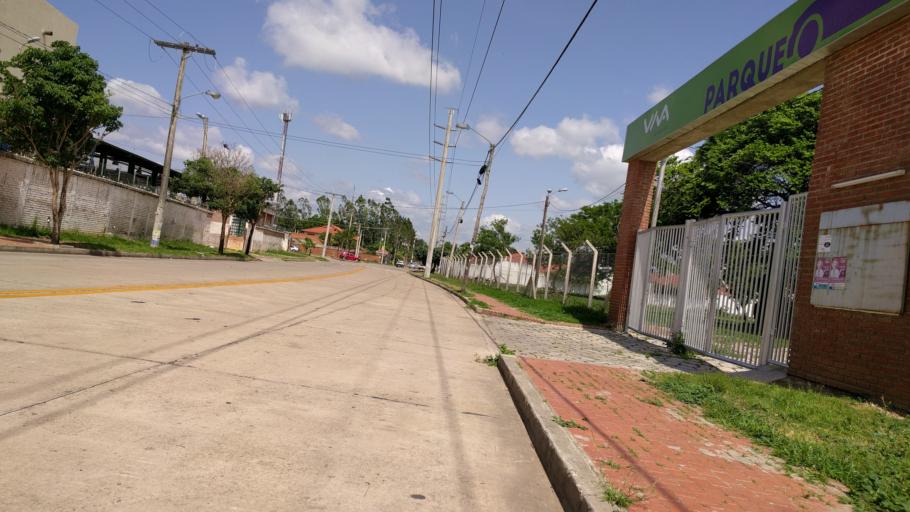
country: BO
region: Santa Cruz
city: Santa Cruz de la Sierra
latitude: -17.7827
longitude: -63.2101
